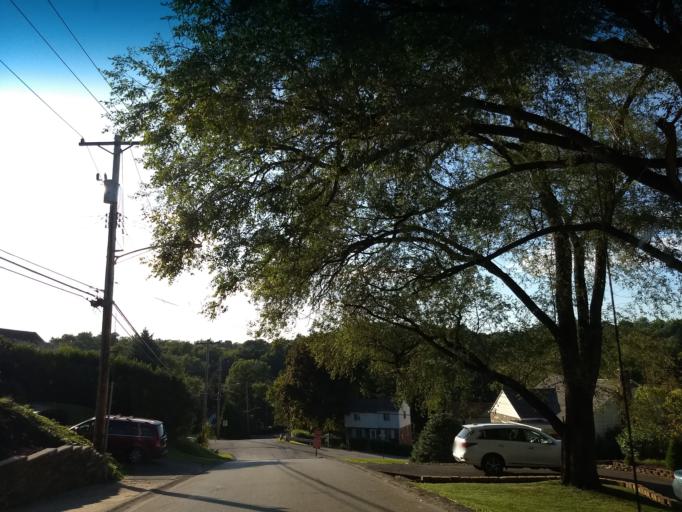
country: US
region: Pennsylvania
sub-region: Allegheny County
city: Mount Lebanon
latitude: 40.3471
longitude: -80.0324
